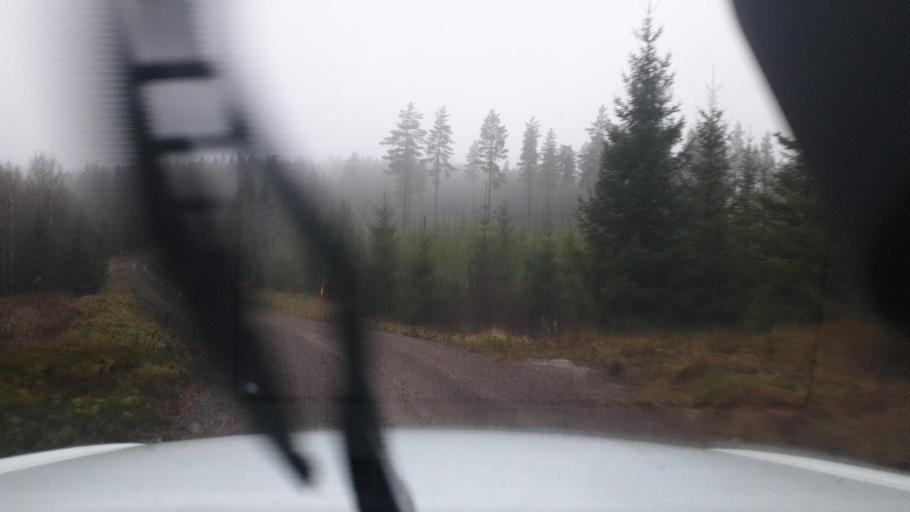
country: SE
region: Vaermland
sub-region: Torsby Kommun
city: Torsby
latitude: 59.9467
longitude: 12.7946
